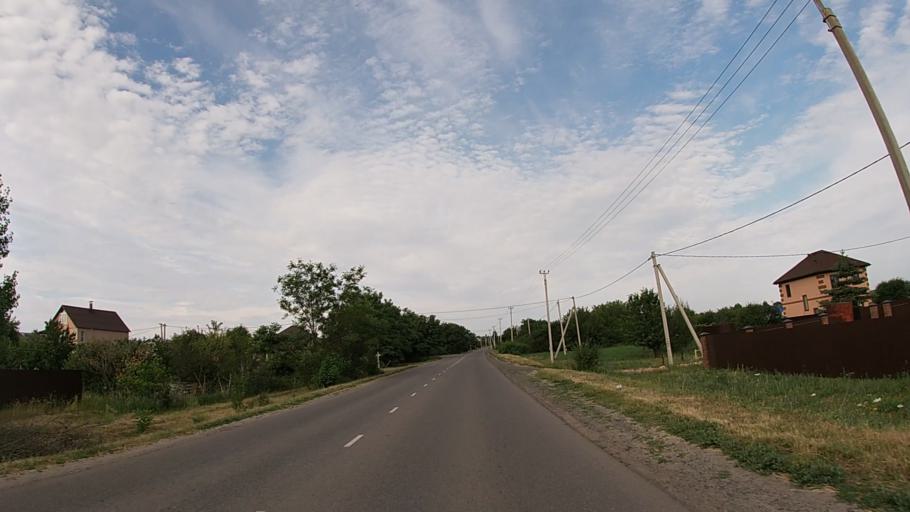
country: RU
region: Belgorod
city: Severnyy
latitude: 50.6961
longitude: 36.5733
